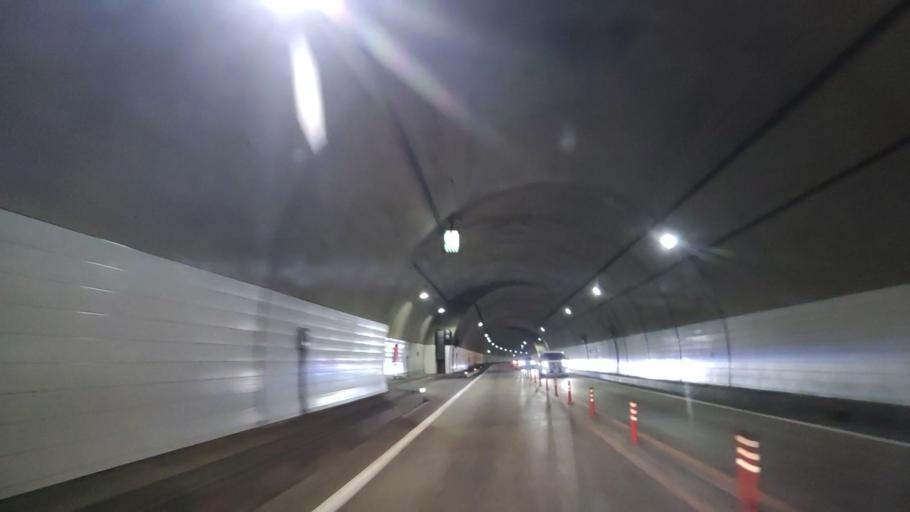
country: JP
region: Akita
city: Odate
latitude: 40.3631
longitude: 140.6961
